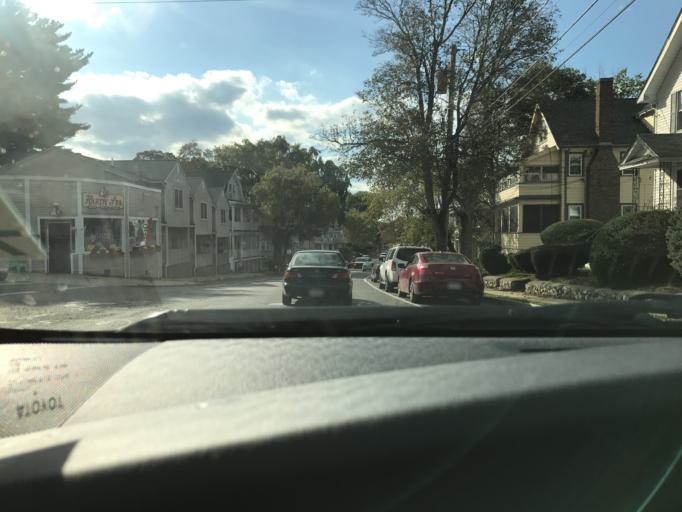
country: US
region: Massachusetts
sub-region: Middlesex County
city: Watertown
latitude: 42.3802
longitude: -71.1800
